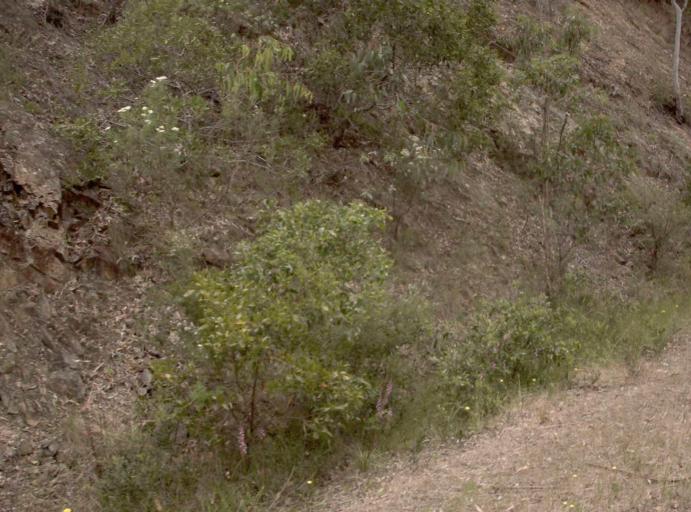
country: AU
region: Victoria
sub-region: East Gippsland
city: Bairnsdale
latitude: -37.6390
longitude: 147.2480
